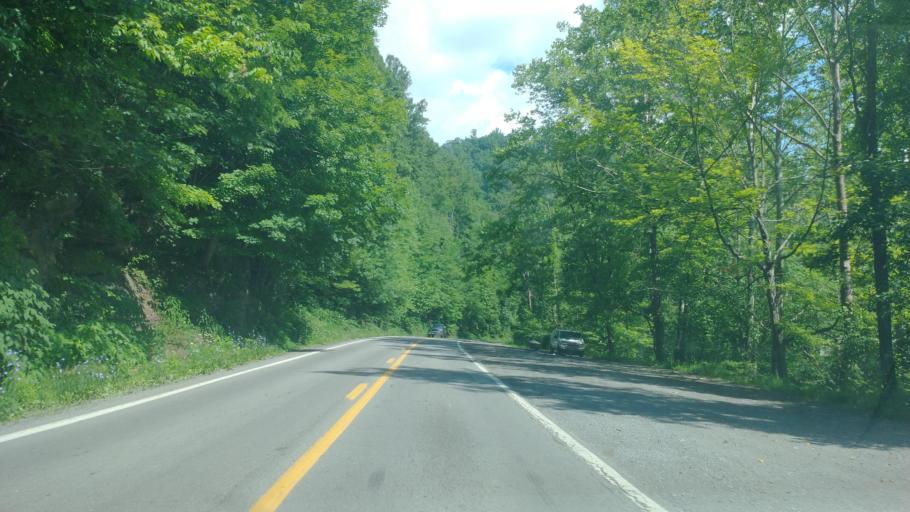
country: US
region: West Virginia
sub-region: McDowell County
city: Welch
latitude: 37.4274
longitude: -81.5517
